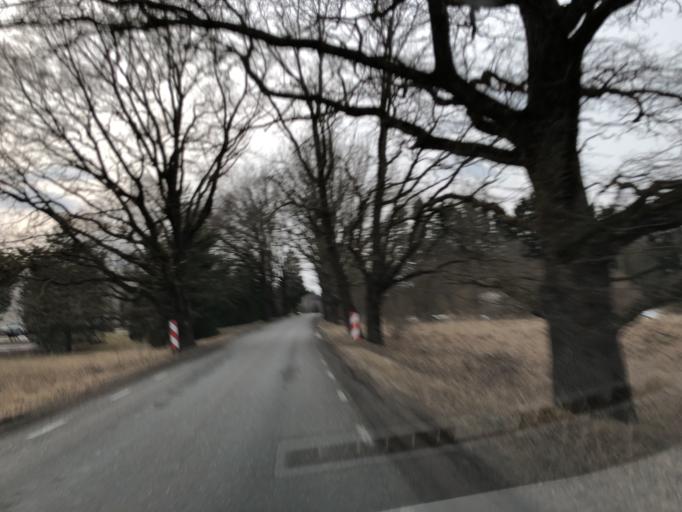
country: EE
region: Paernumaa
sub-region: Vaendra vald (alev)
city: Vandra
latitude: 58.6667
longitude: 25.0190
